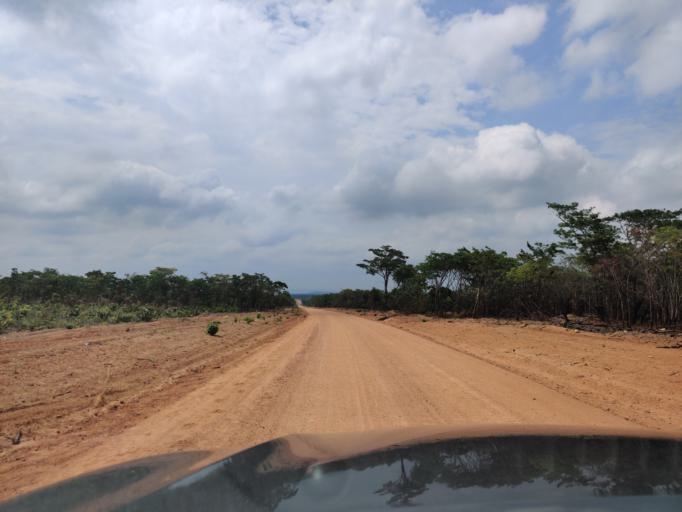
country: ZM
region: Central
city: Mkushi
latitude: -13.6711
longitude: 29.7514
